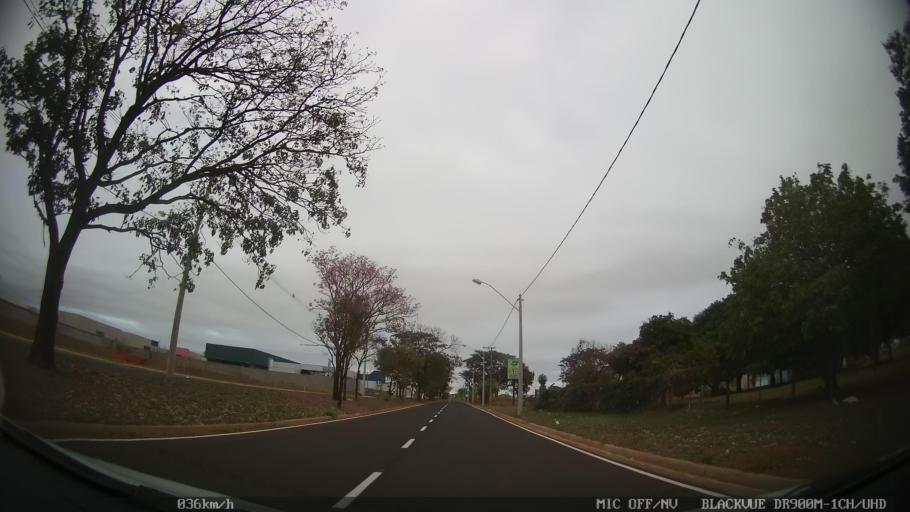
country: BR
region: Sao Paulo
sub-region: Sao Jose Do Rio Preto
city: Sao Jose do Rio Preto
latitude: -20.8245
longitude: -49.4203
